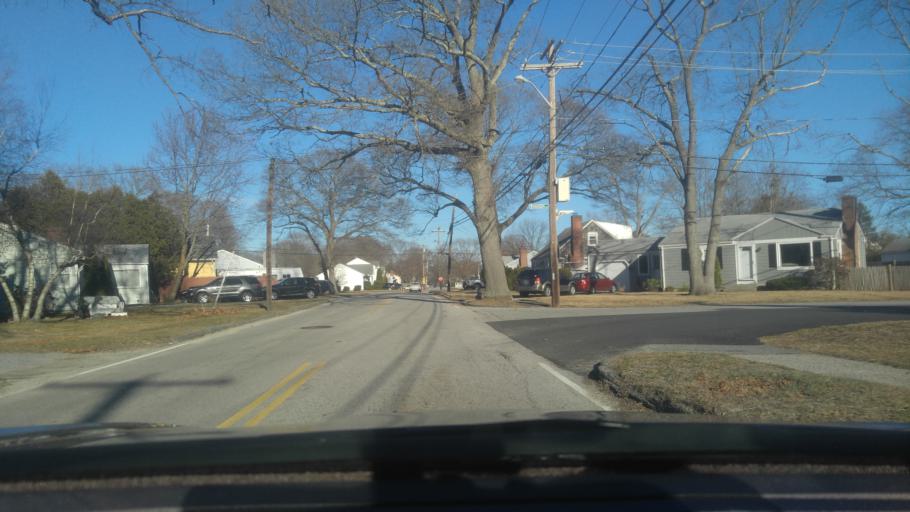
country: US
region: Rhode Island
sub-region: Kent County
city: Warwick
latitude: 41.6964
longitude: -71.4295
